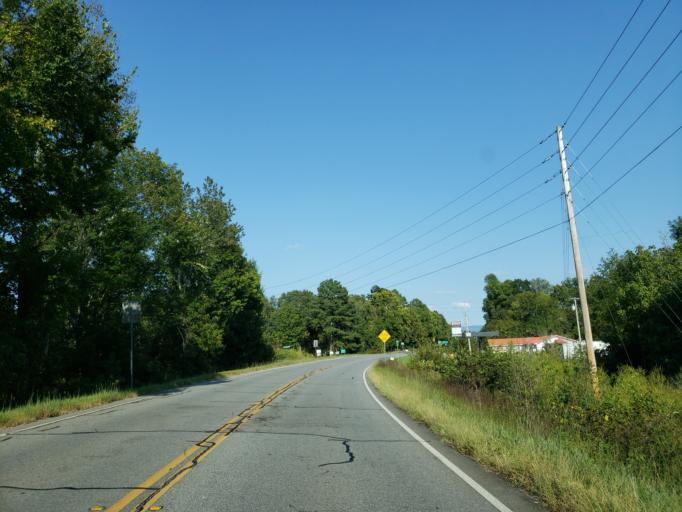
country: US
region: Georgia
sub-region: Whitfield County
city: Varnell
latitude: 34.9211
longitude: -84.8439
